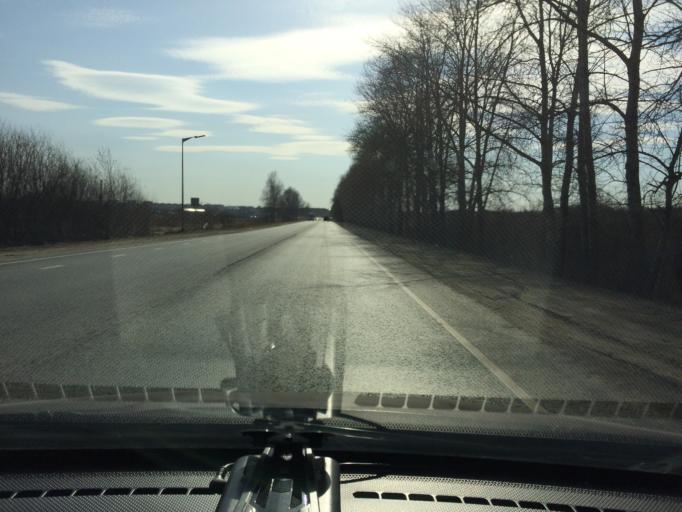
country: RU
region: Mariy-El
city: Yoshkar-Ola
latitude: 56.6527
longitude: 47.9519
